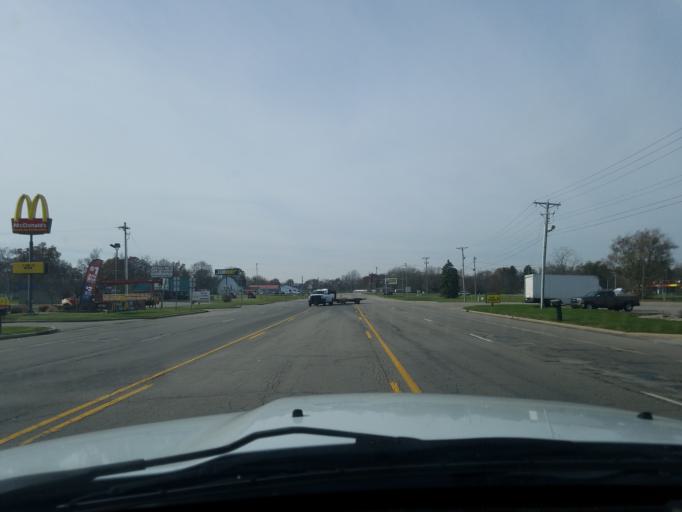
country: US
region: Indiana
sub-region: Delaware County
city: Daleville
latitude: 40.1139
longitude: -85.5731
